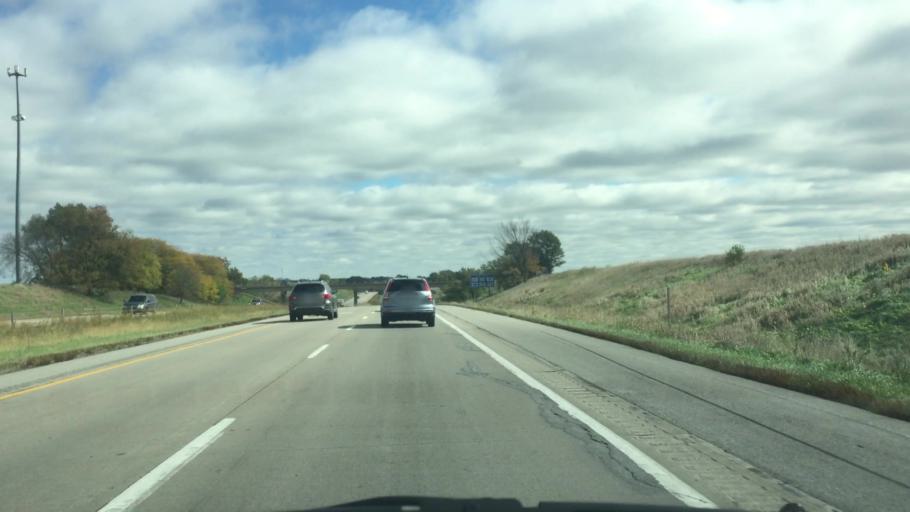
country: US
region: Iowa
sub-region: Jasper County
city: Newton
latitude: 41.6832
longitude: -93.1433
